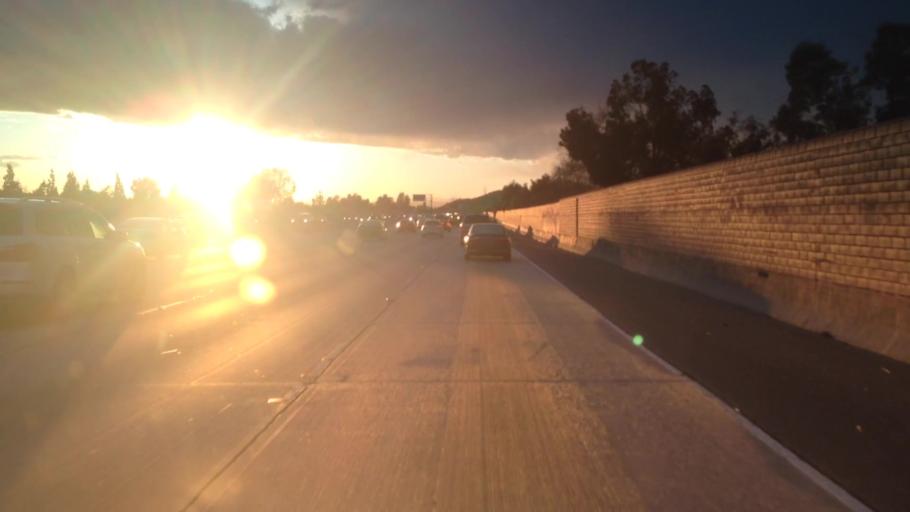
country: US
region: California
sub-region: Los Angeles County
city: San Dimas
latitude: 34.1200
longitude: -117.7954
